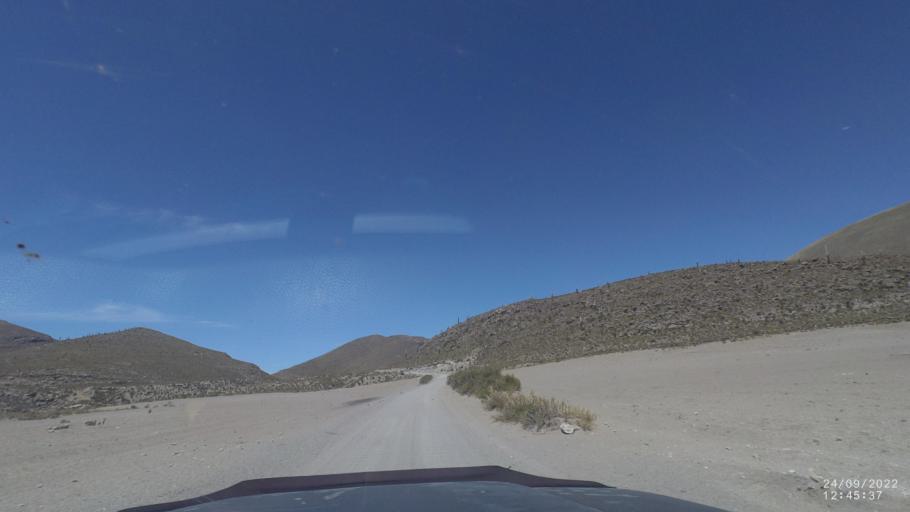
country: BO
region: Potosi
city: Colchani
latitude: -19.7999
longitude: -67.5761
